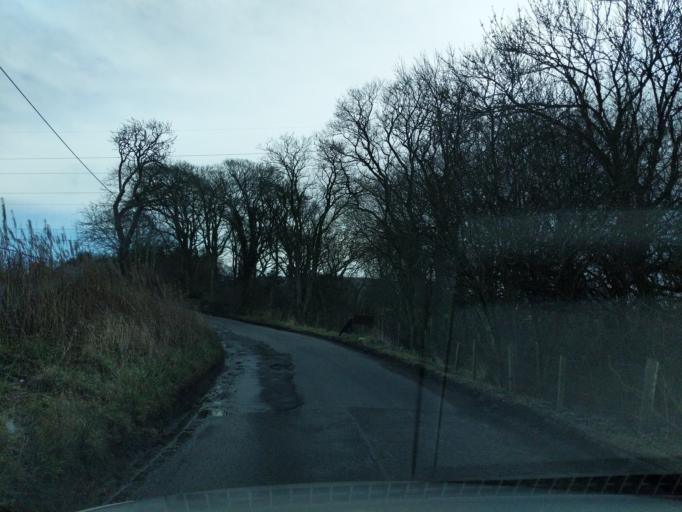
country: GB
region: Scotland
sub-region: Edinburgh
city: Balerno
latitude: 55.8764
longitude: -3.3238
